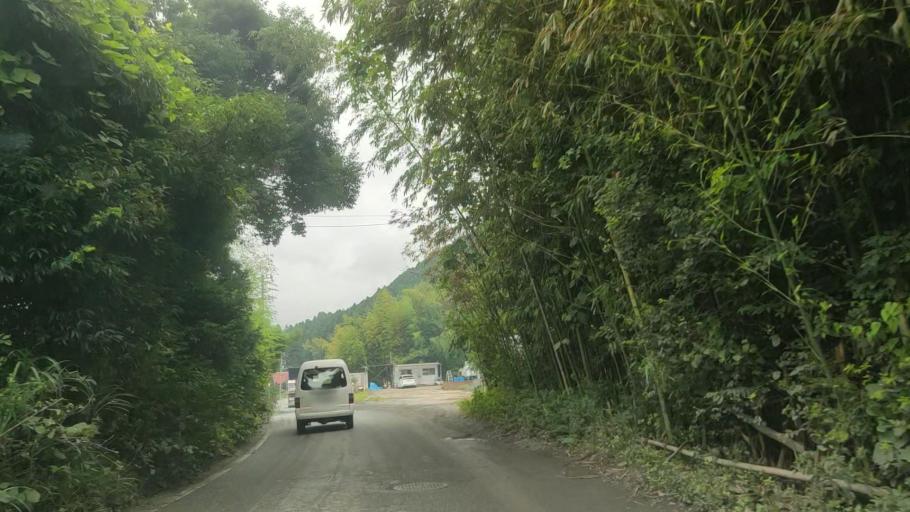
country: JP
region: Shizuoka
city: Fujinomiya
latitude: 35.2165
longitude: 138.5440
